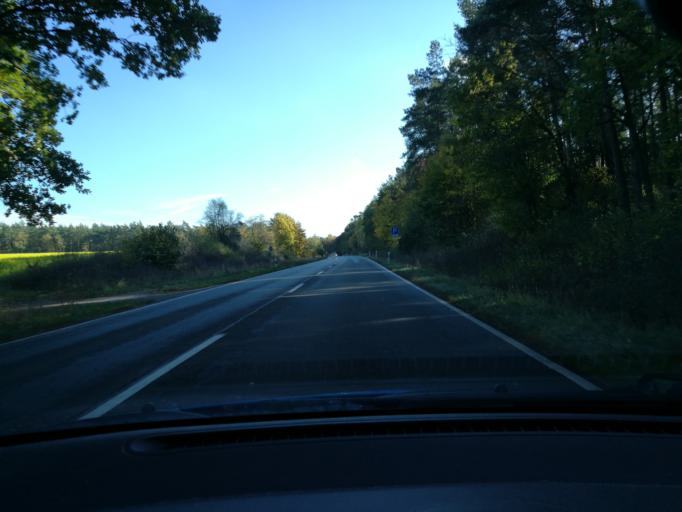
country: DE
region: Lower Saxony
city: Thomasburg
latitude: 53.1921
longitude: 10.6543
